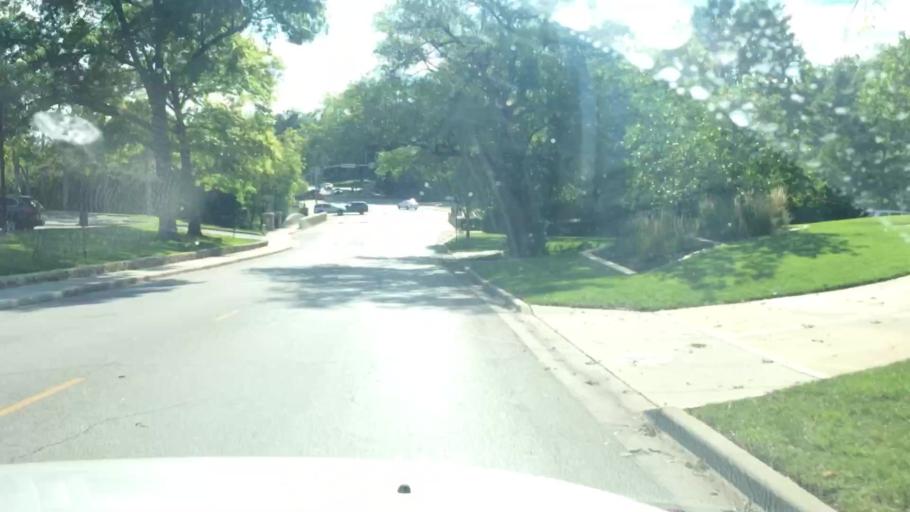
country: US
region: Kansas
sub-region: Johnson County
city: Mission Hills
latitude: 39.0064
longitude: -94.6268
